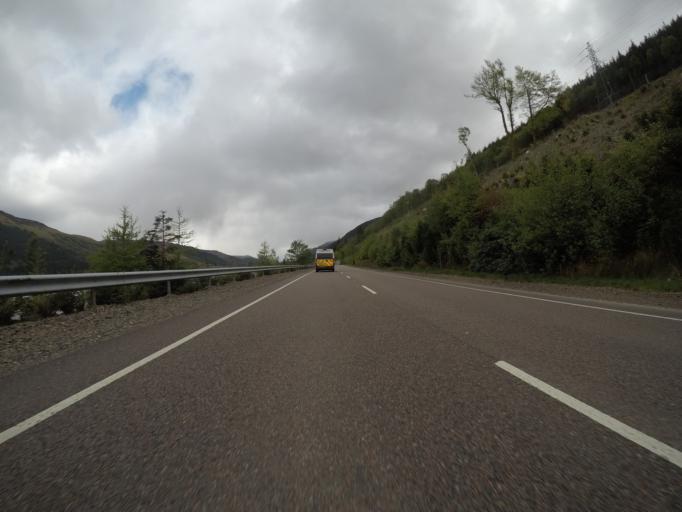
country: GB
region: Scotland
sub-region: Highland
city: Spean Bridge
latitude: 57.0032
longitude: -4.8481
